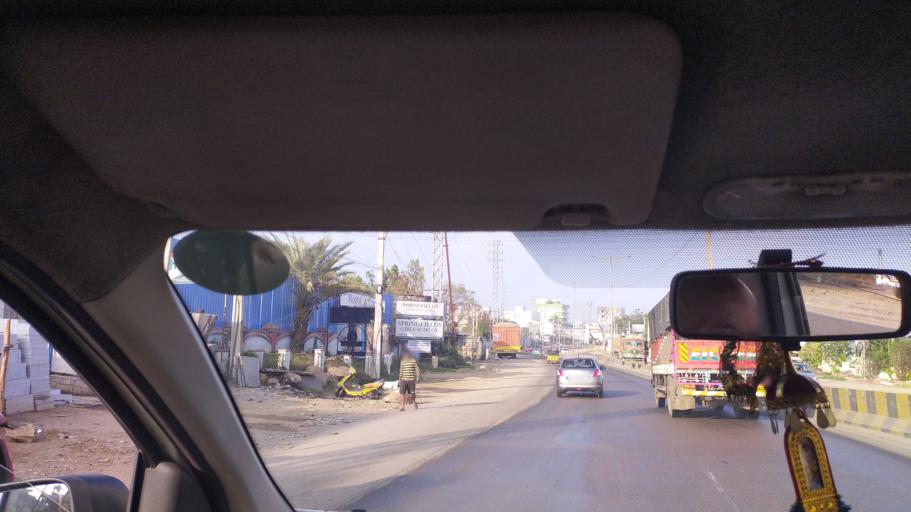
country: IN
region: Telangana
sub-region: Rangareddi
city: Balapur
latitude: 17.3144
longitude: 78.4618
